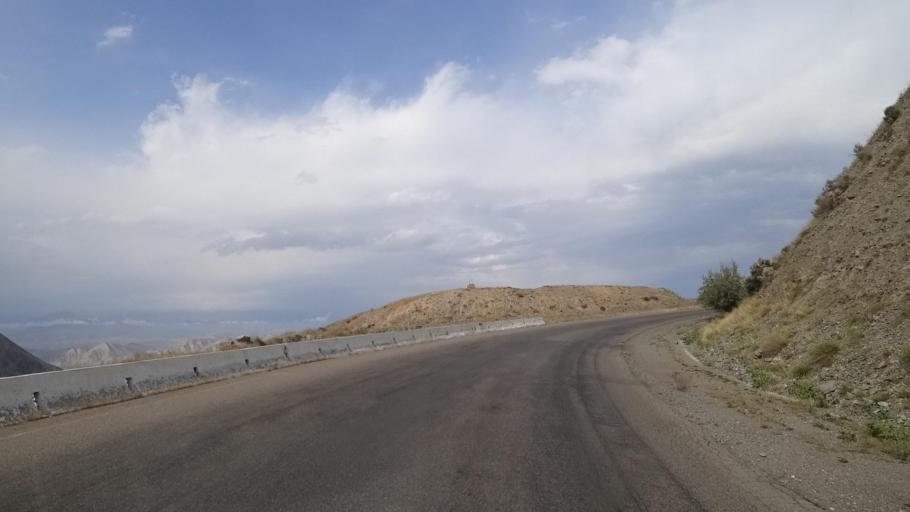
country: KG
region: Jalal-Abad
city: Uch-Terek
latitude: 41.7639
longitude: 73.0586
